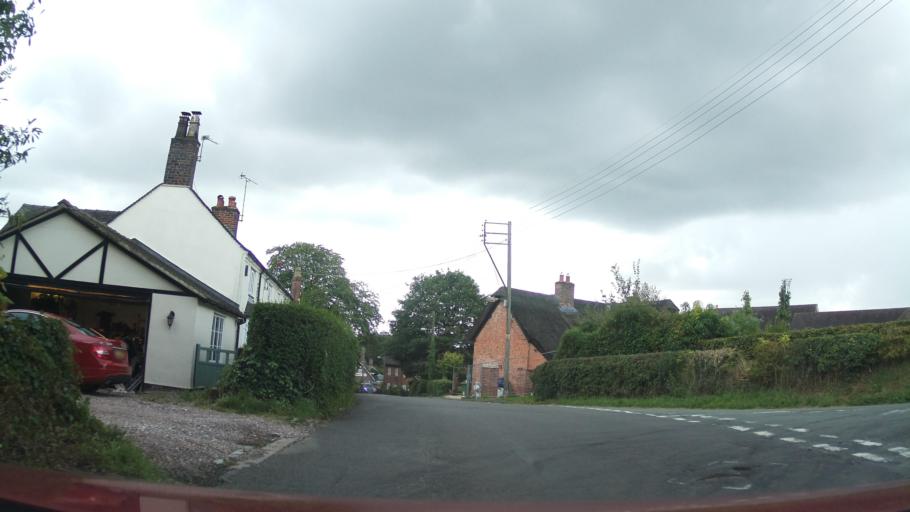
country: GB
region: England
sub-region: Staffordshire
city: Barlaston
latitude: 52.9190
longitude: -2.2213
